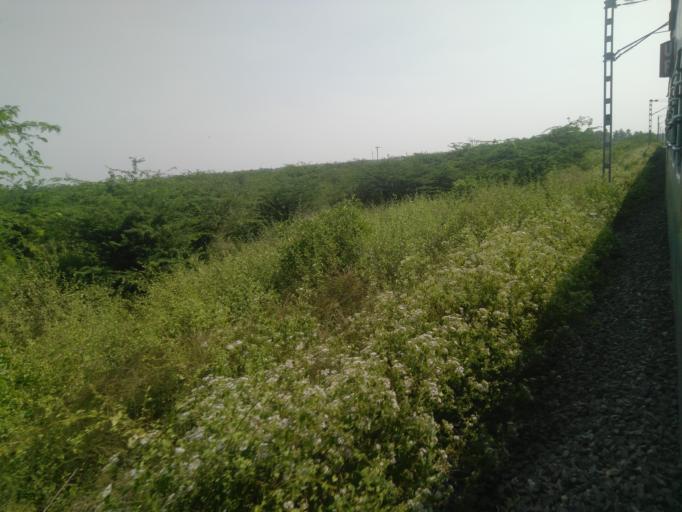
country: IN
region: Tamil Nadu
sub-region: Coimbatore
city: Periyanayakkanpalaiyam
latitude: 11.1227
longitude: 76.9486
